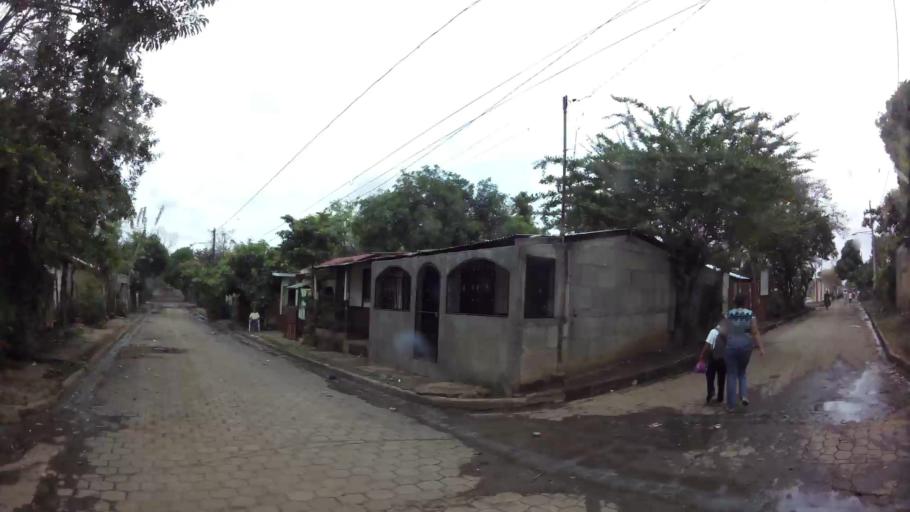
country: NI
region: Granada
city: Nandaime
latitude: 11.7544
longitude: -86.0565
